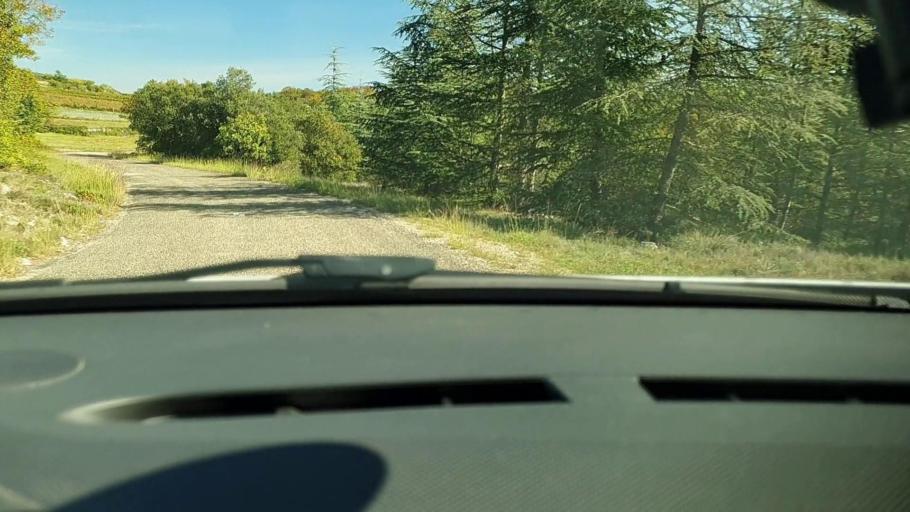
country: FR
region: Languedoc-Roussillon
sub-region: Departement du Gard
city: Barjac
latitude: 44.1930
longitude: 4.3177
